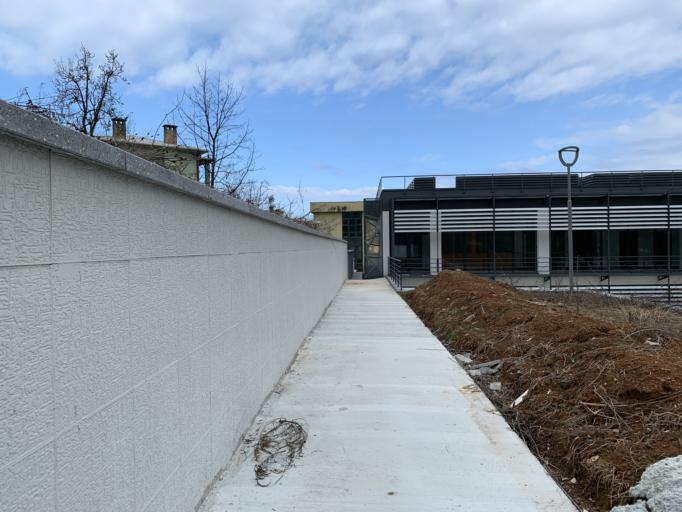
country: TR
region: Trabzon
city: Trabzon
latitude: 40.9900
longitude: 39.7749
